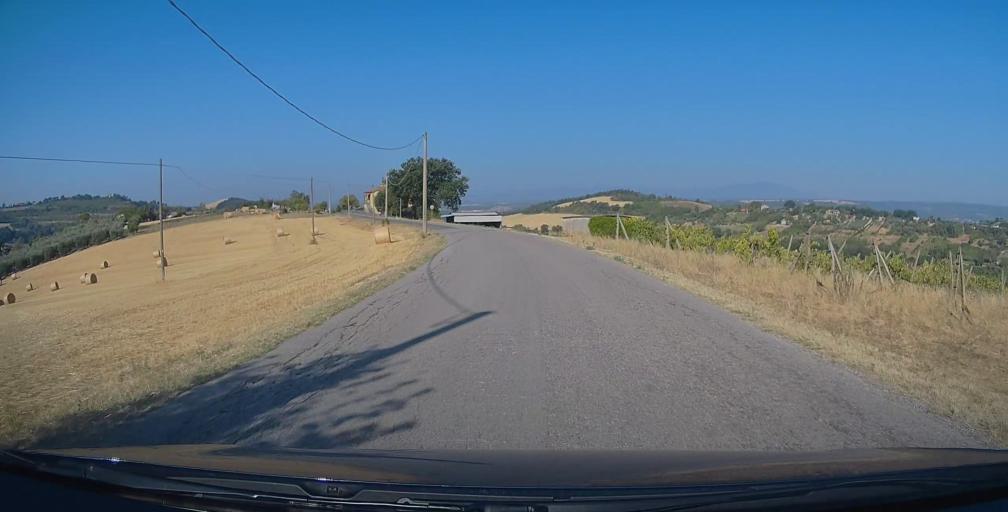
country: IT
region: Umbria
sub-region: Provincia di Terni
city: Otricoli
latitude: 42.4067
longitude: 12.4994
